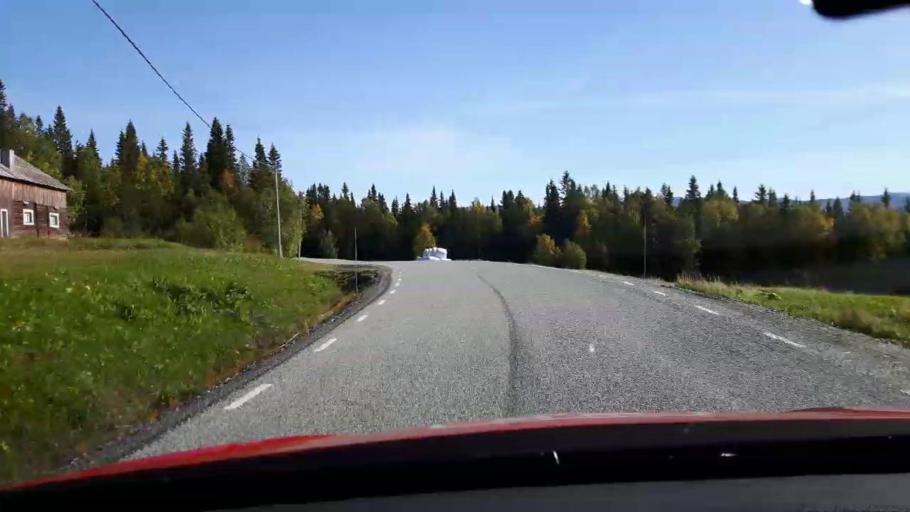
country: NO
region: Nord-Trondelag
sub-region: Royrvik
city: Royrvik
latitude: 64.8149
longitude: 14.1477
